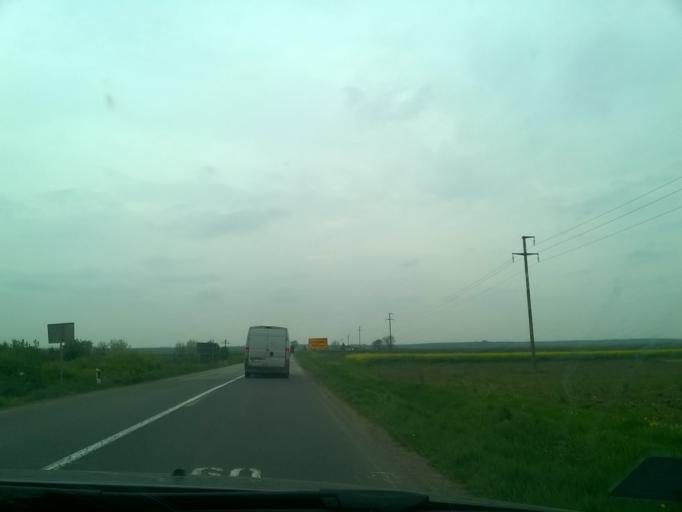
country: RS
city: Platicevo
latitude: 44.8193
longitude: 19.7784
